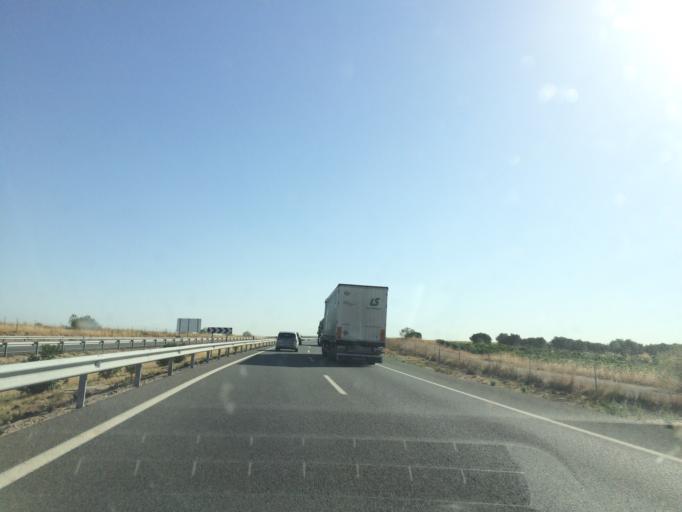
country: ES
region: Castille-La Mancha
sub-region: Province of Toledo
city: La Torre de Esteban Hambran
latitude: 40.1678
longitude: -4.1655
